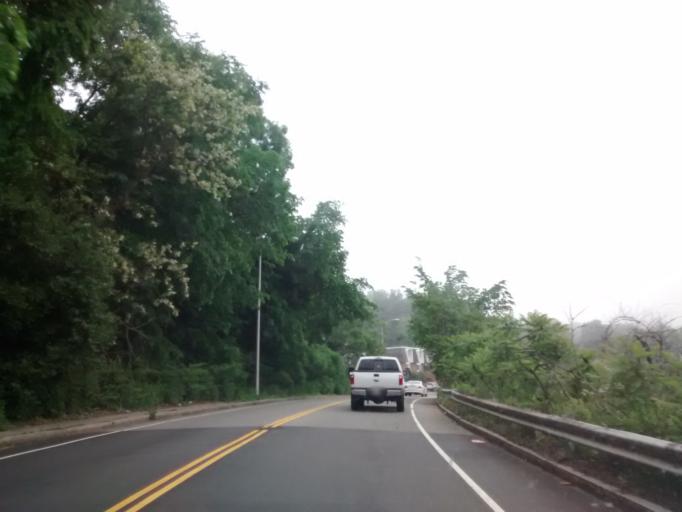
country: US
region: Massachusetts
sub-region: Worcester County
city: Worcester
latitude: 42.2893
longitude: -71.7966
